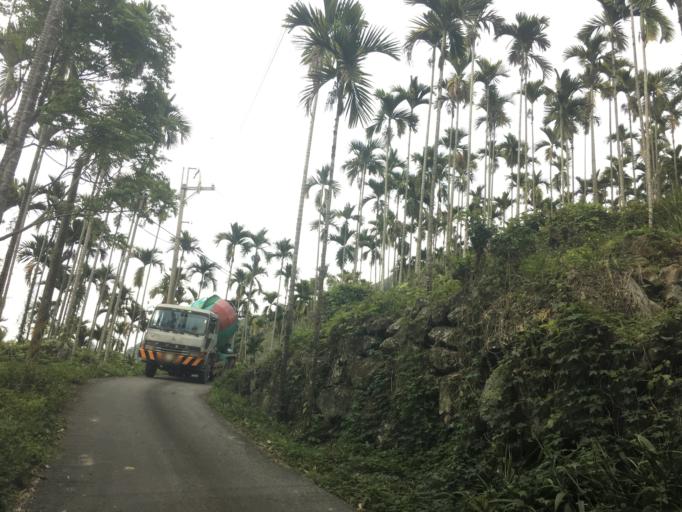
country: TW
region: Taiwan
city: Zhongxing New Village
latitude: 23.9732
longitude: 120.8201
